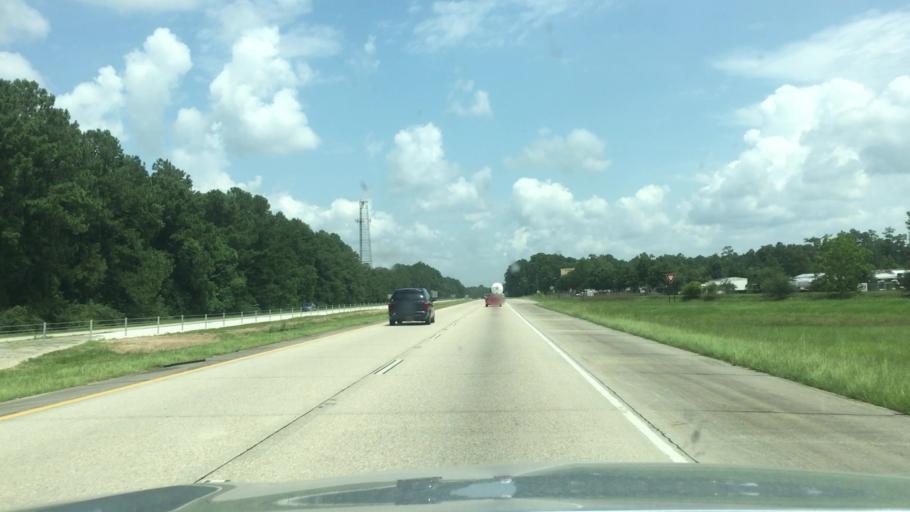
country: US
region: Louisiana
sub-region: Saint Tammany Parish
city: Pearl River
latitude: 30.3536
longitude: -89.7405
